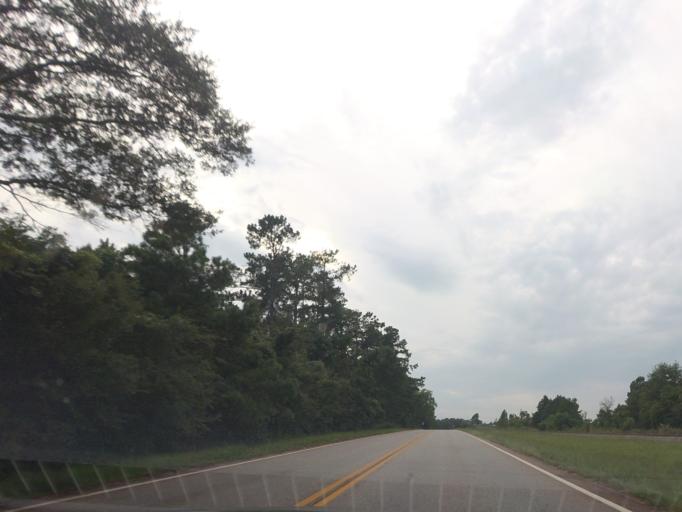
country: US
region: Georgia
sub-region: Twiggs County
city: Jeffersonville
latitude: 32.7174
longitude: -83.3957
